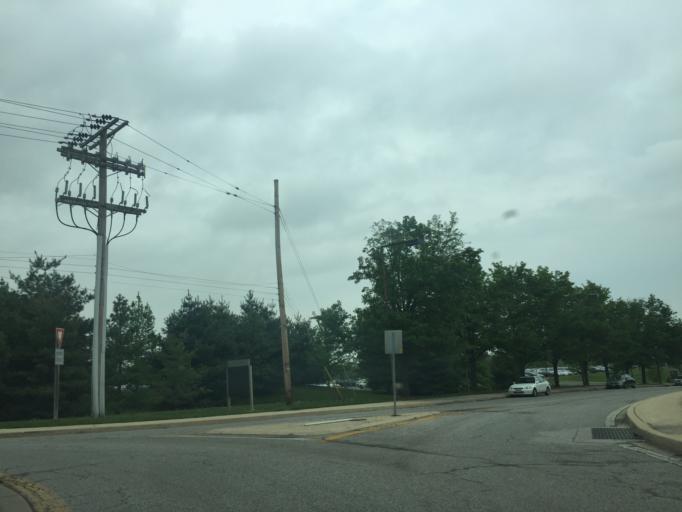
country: US
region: Maryland
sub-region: Baltimore County
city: Charlestown
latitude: 39.2571
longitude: -76.7196
